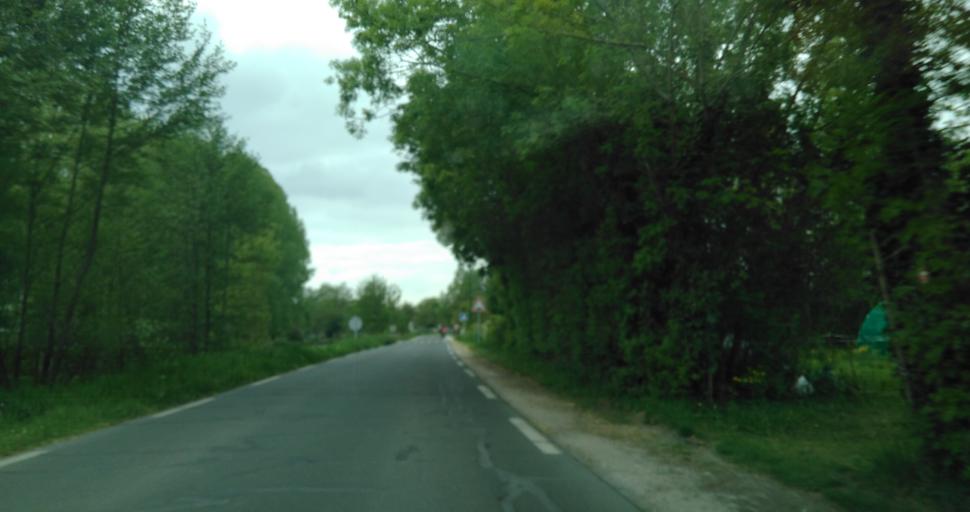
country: FR
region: Poitou-Charentes
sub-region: Departement des Deux-Sevres
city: Coulon
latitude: 46.3149
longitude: -0.6043
